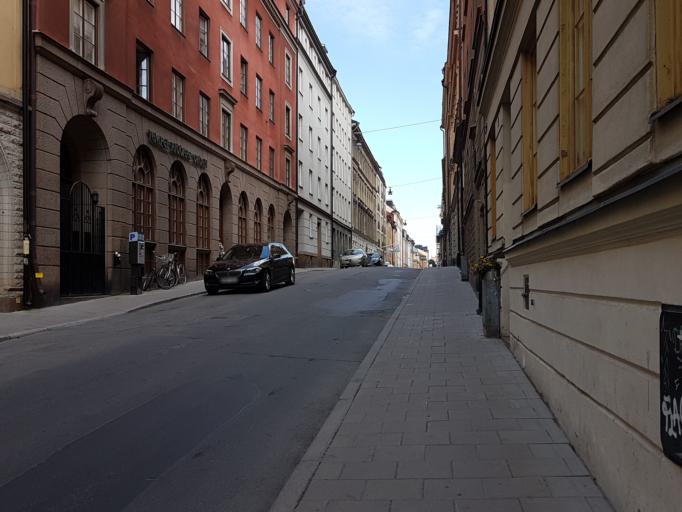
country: SE
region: Stockholm
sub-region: Stockholms Kommun
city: Stockholm
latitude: 59.3372
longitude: 18.0544
